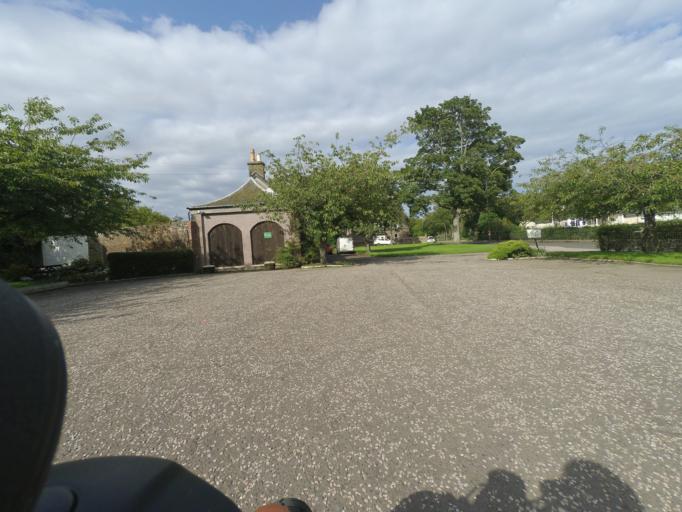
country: GB
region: Scotland
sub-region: Angus
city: Montrose
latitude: 56.7135
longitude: -2.4632
